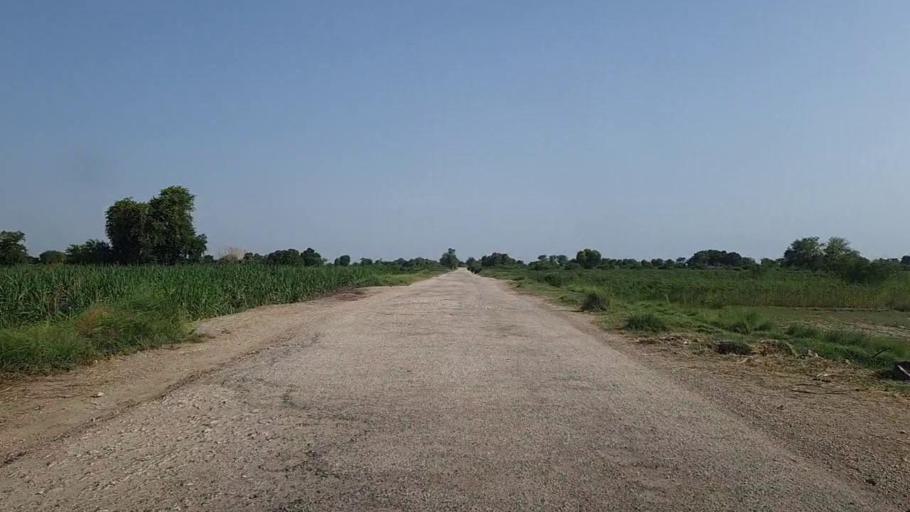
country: PK
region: Sindh
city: Karaundi
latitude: 26.8743
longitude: 68.3283
